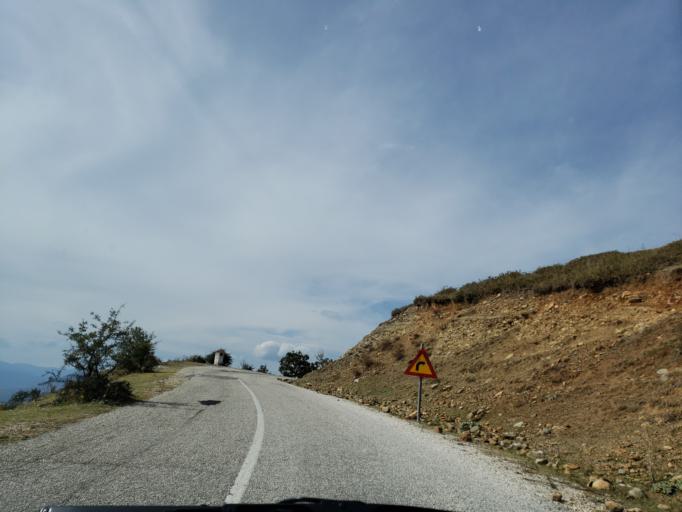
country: GR
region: Thessaly
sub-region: Trikala
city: Kastraki
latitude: 39.7521
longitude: 21.6611
